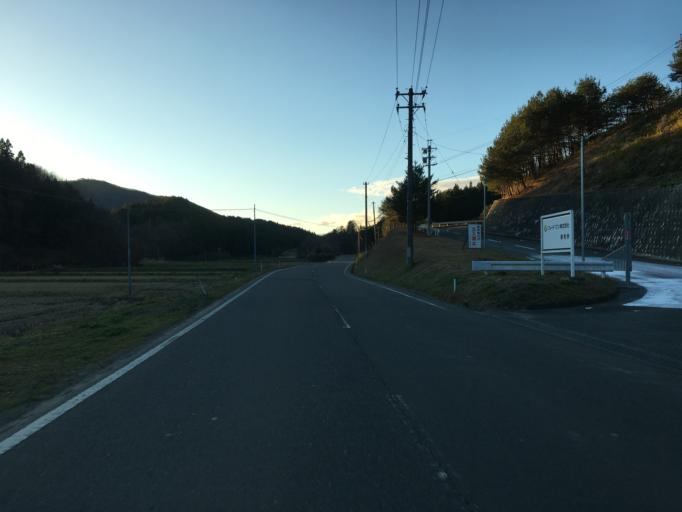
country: JP
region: Fukushima
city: Ishikawa
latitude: 37.2730
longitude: 140.5727
